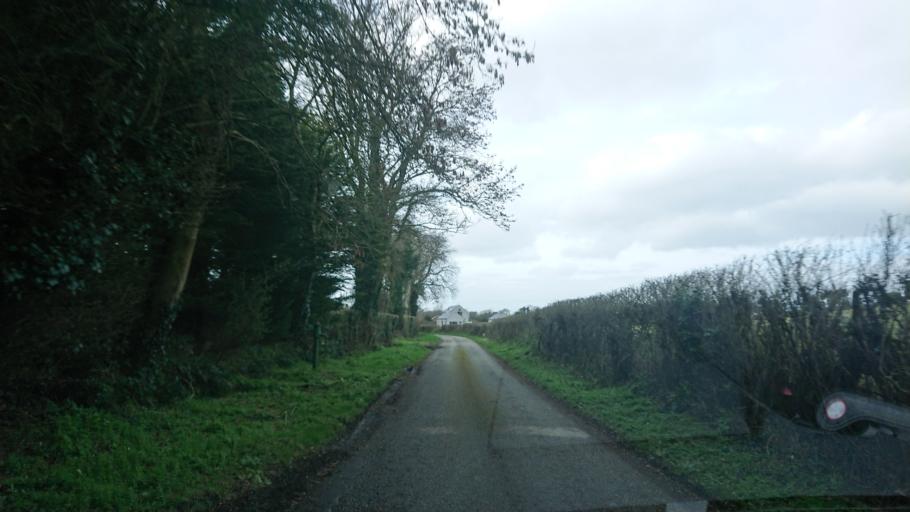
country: IE
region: Leinster
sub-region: Kildare
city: Eadestown
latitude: 53.1700
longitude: -6.6184
